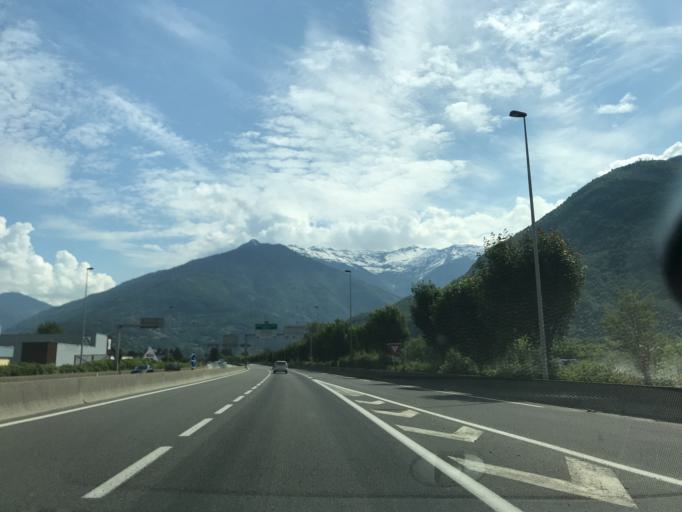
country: FR
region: Rhone-Alpes
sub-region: Departement de la Savoie
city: Grignon
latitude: 45.6557
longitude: 6.3703
